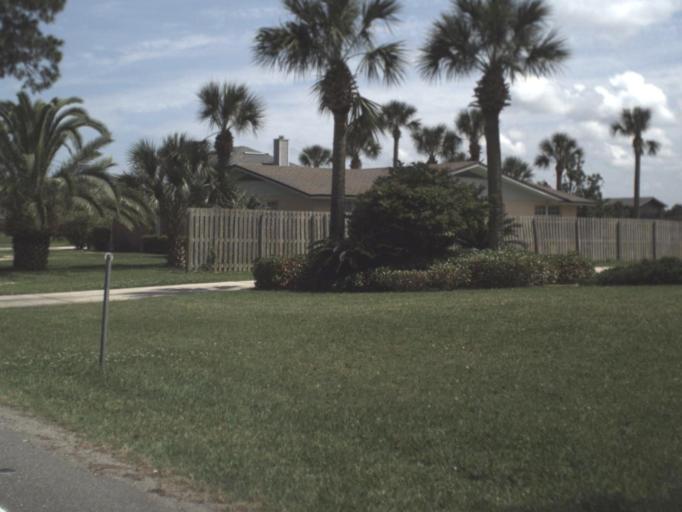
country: US
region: Florida
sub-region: Duval County
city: Jacksonville
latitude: 30.4164
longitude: -81.5282
